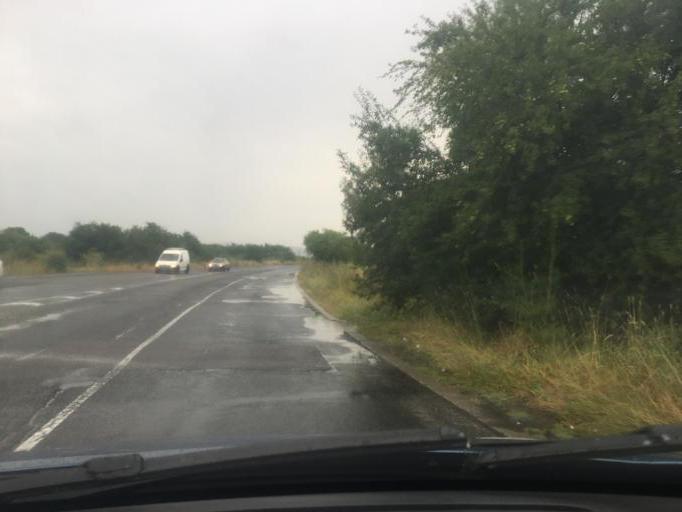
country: BG
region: Burgas
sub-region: Obshtina Burgas
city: Burgas
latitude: 42.5546
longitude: 27.4910
